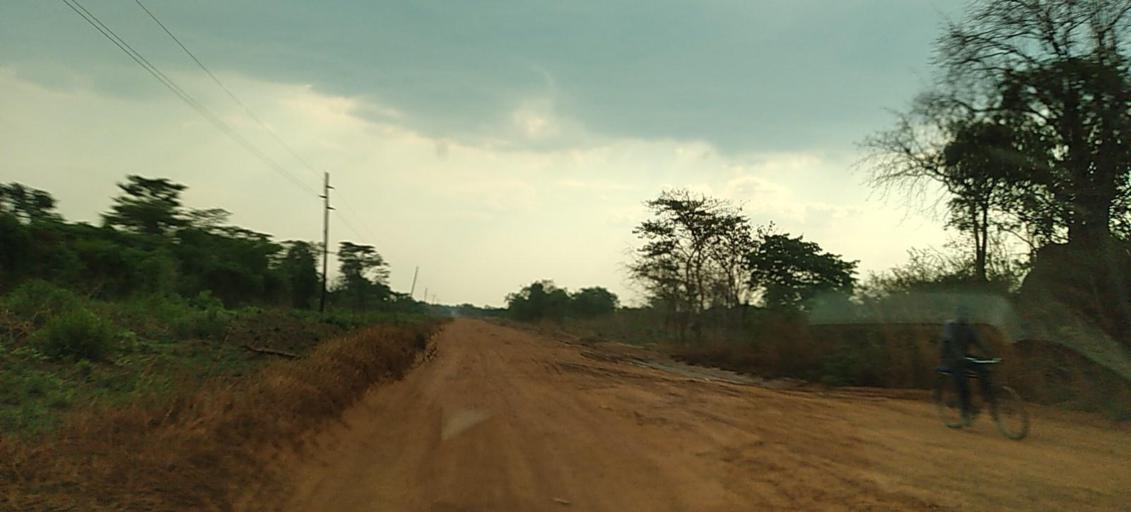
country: ZM
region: Copperbelt
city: Kalulushi
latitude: -12.9458
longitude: 27.9165
